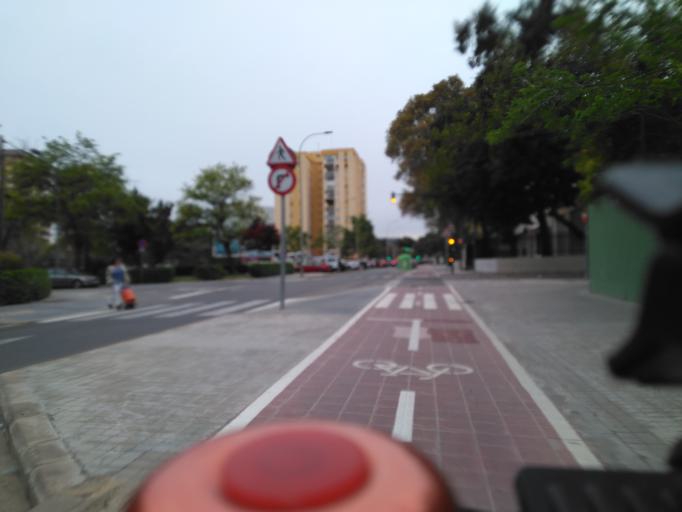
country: ES
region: Valencia
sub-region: Provincia de Valencia
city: Mislata
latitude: 39.4668
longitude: -0.4032
